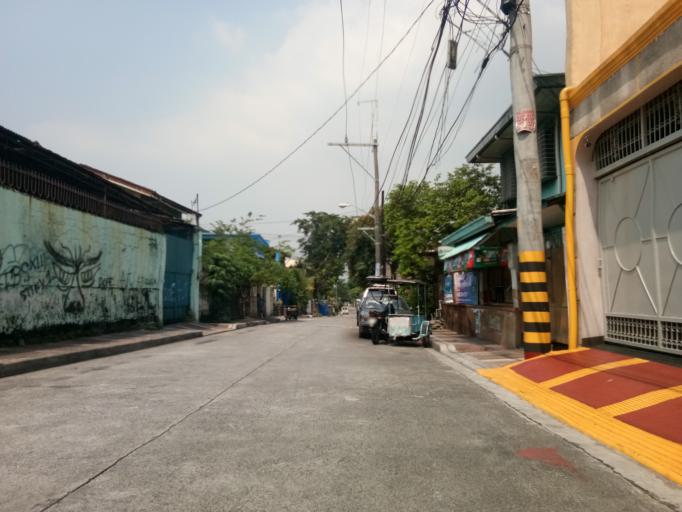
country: PH
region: Metro Manila
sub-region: Marikina
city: Calumpang
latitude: 14.6169
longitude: 121.0617
